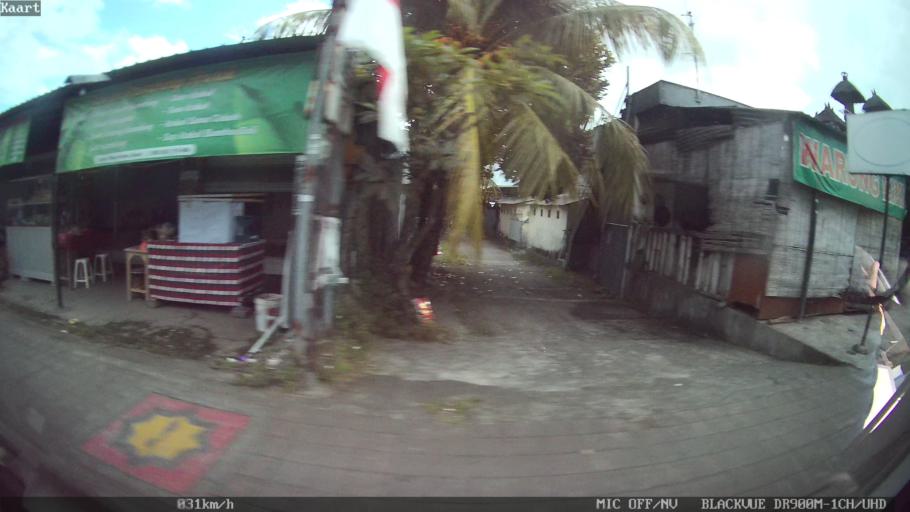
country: ID
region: Bali
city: Banjar Pekenjelodan
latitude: -8.5816
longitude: 115.1809
